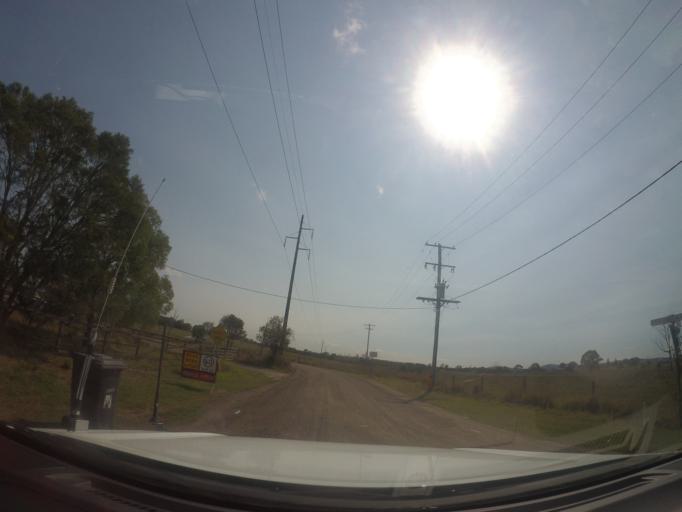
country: AU
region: Queensland
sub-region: Logan
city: Chambers Flat
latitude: -27.7664
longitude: 153.0627
